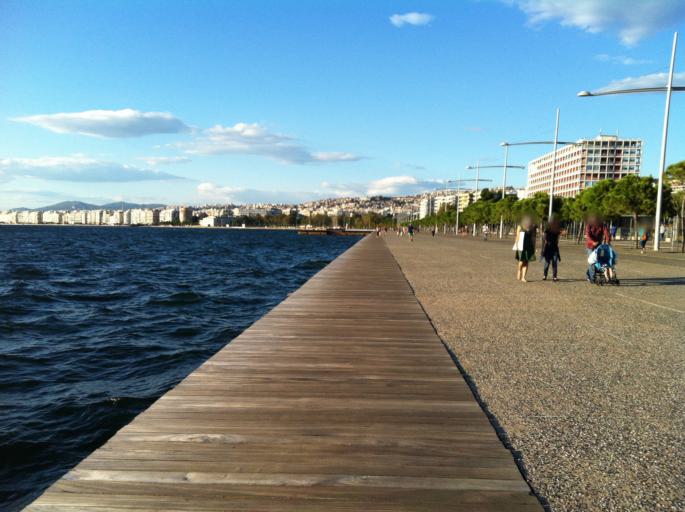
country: GR
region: Central Macedonia
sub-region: Nomos Thessalonikis
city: Triandria
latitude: 40.6157
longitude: 22.9512
